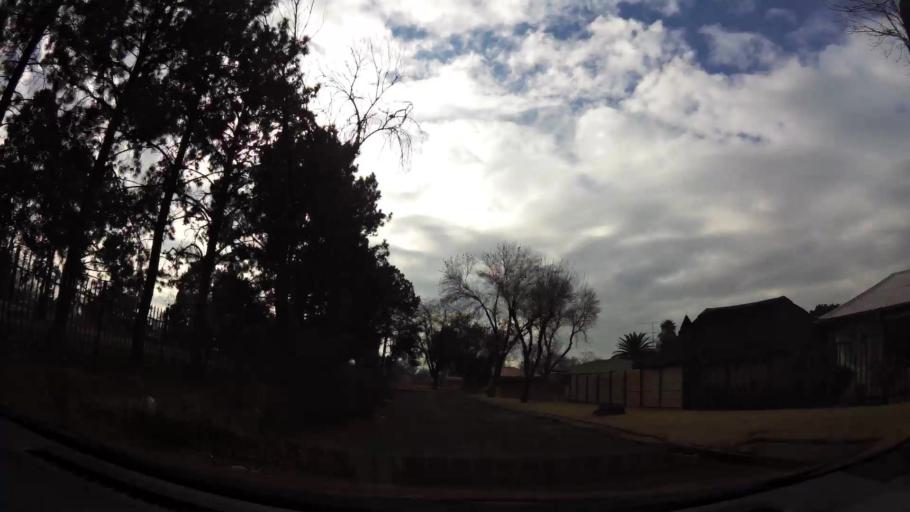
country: ZA
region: Gauteng
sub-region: Sedibeng District Municipality
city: Vanderbijlpark
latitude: -26.7010
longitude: 27.8280
